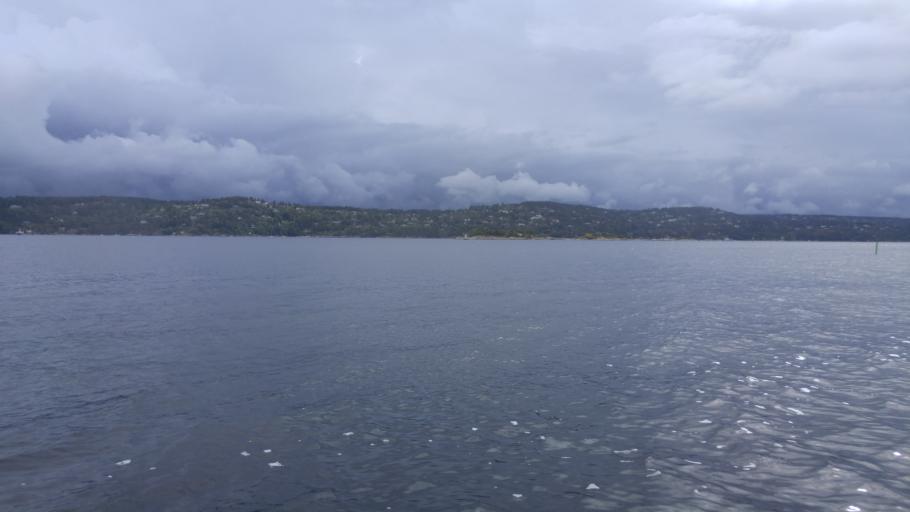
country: NO
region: Akershus
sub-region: Nesodden
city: Fagerstrand
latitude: 59.7044
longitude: 10.5698
